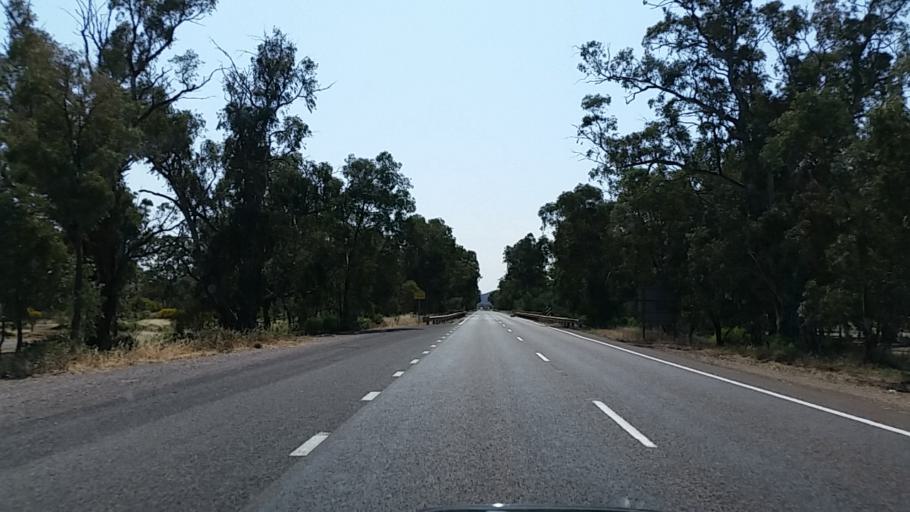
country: AU
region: South Australia
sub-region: Port Pirie City and Dists
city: Port Pirie
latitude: -32.8473
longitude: 137.9818
